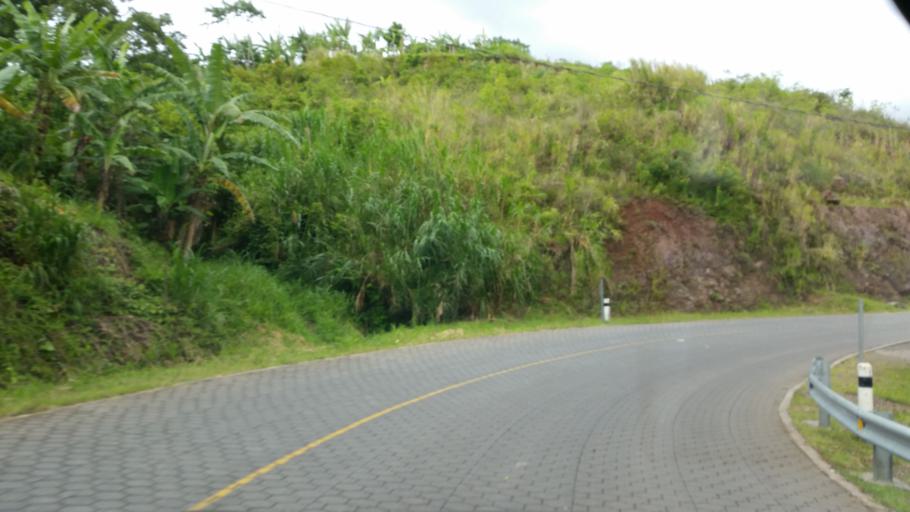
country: NI
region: Jinotega
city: Jinotega
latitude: 13.2081
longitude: -85.7180
